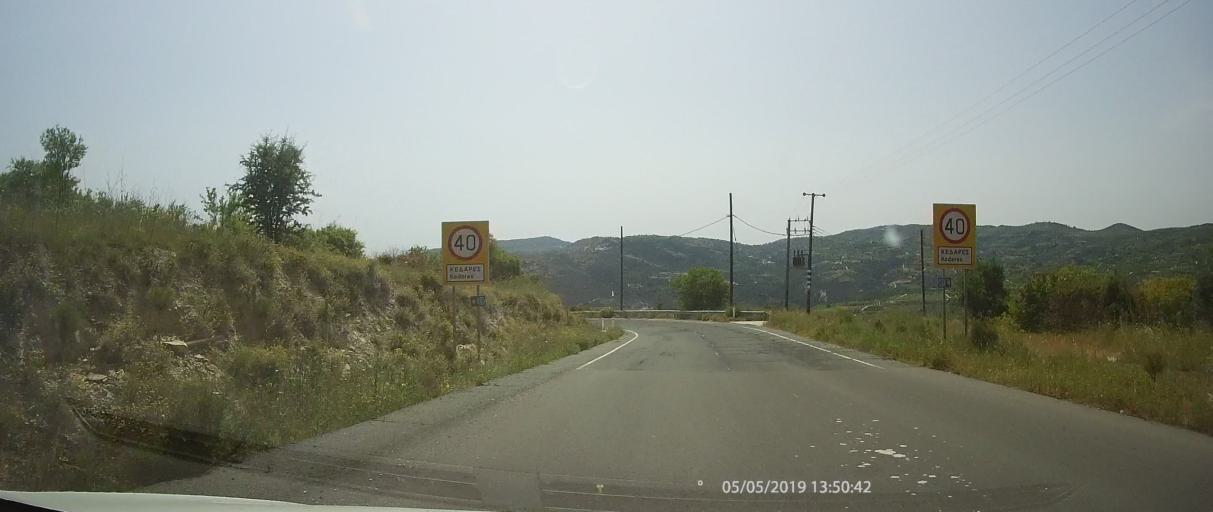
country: CY
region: Limassol
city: Pachna
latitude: 34.8403
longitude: 32.7373
